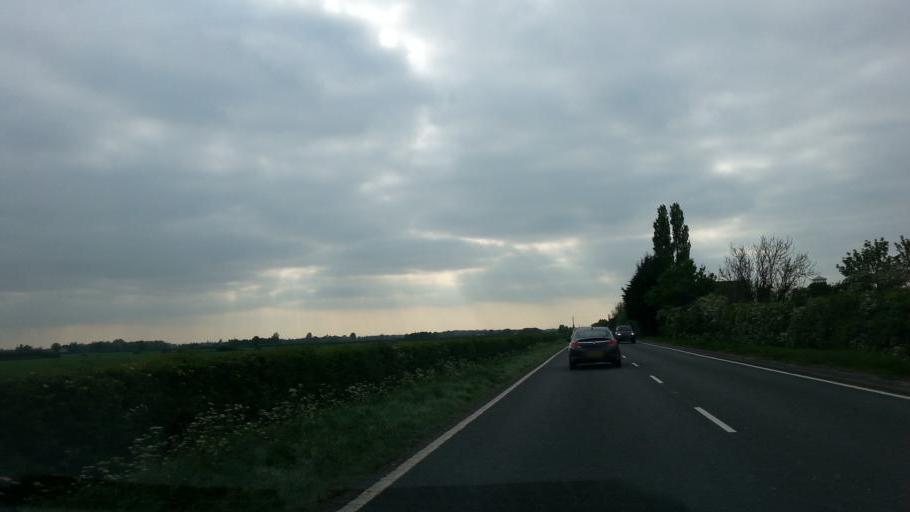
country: GB
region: England
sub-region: Lincolnshire
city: Navenby
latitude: 53.0665
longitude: -0.6239
